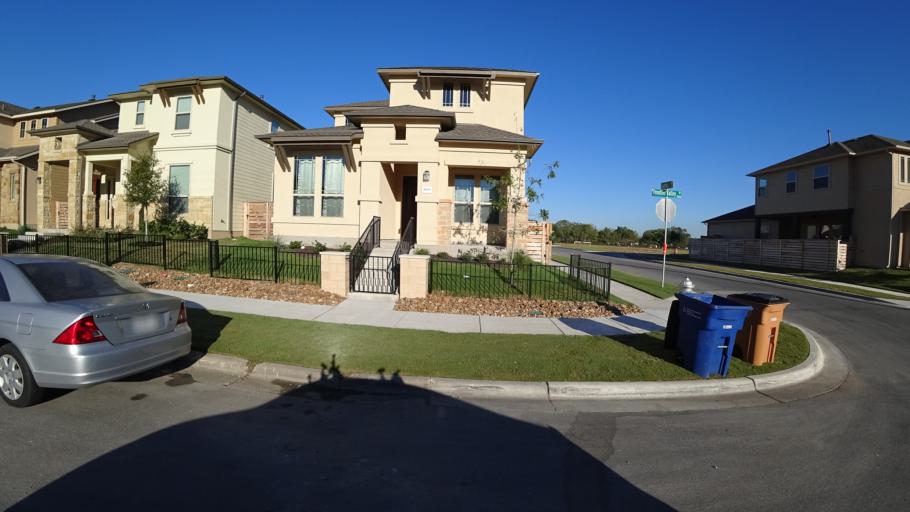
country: US
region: Texas
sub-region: Travis County
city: Austin
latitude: 30.2251
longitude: -97.6951
